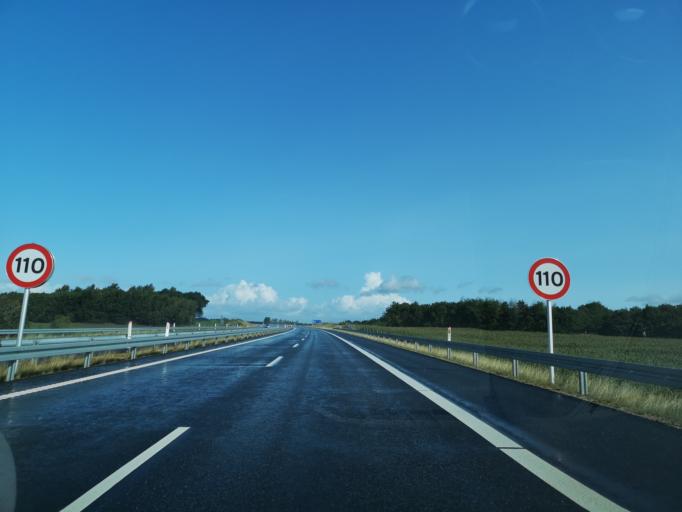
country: DK
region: Central Jutland
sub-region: Herning Kommune
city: Snejbjerg
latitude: 56.1790
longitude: 8.8928
